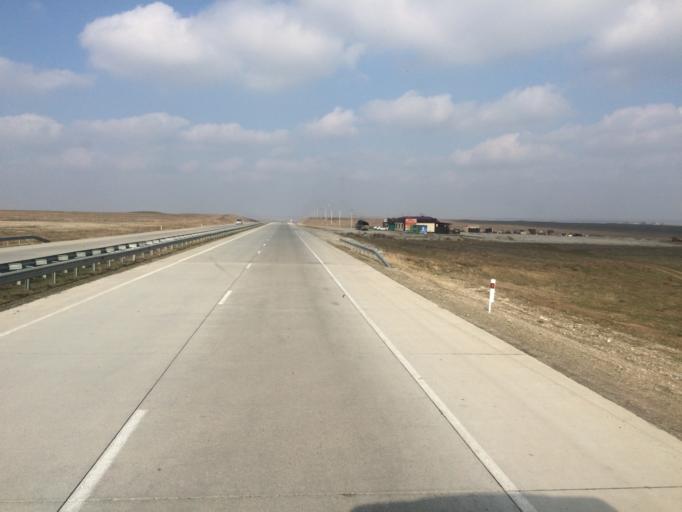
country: KZ
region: Ongtustik Qazaqstan
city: Temirlanovka
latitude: 42.5675
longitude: 69.3108
